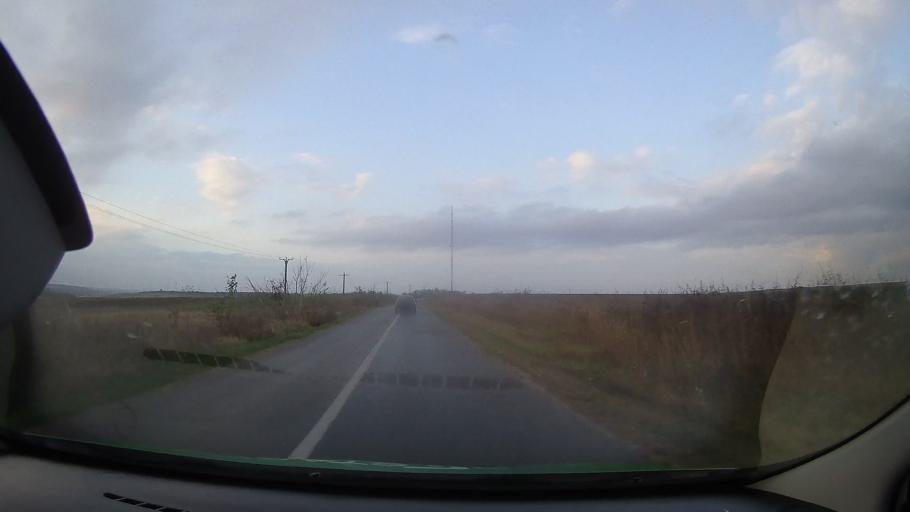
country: RO
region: Constanta
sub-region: Comuna Dobromir
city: Dobromir
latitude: 44.0422
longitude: 27.7559
